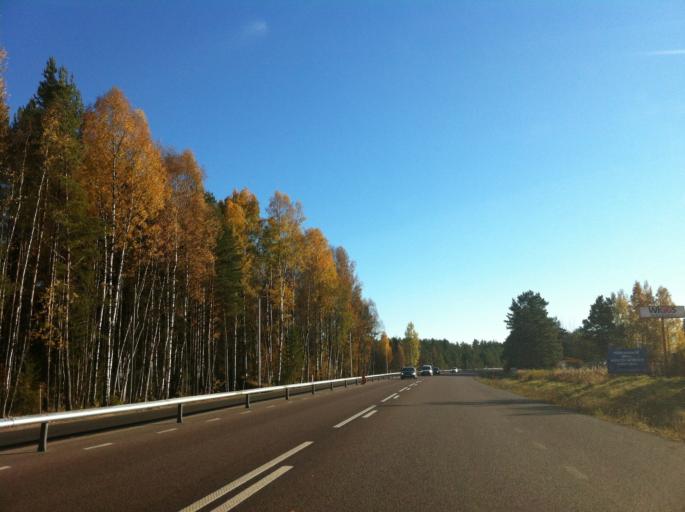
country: SE
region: Dalarna
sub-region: Mora Kommun
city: Mora
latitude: 61.0248
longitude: 14.5336
